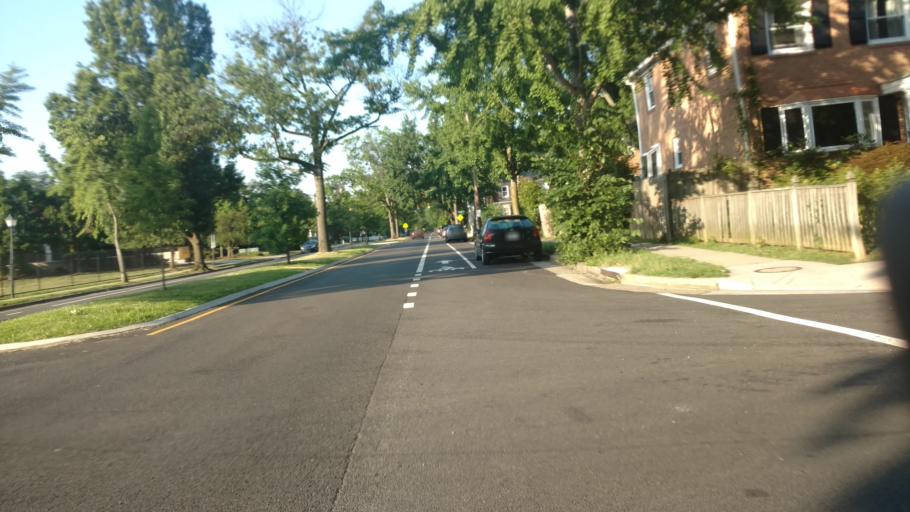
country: US
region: Virginia
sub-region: City of Alexandria
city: Alexandria
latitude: 38.8295
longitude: -77.0602
